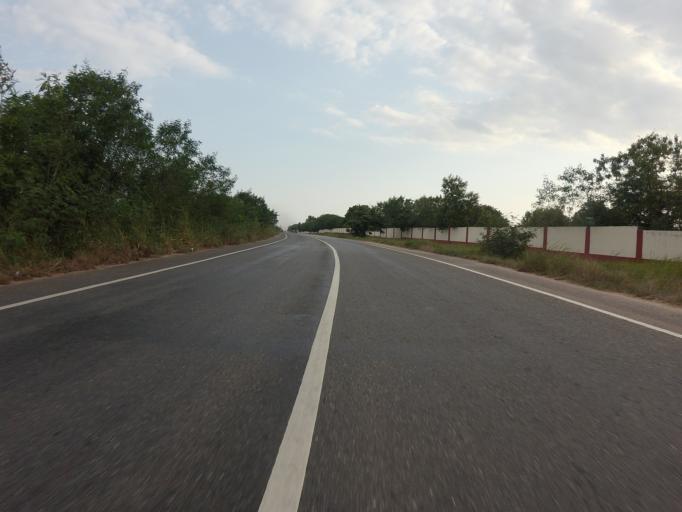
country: GH
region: Volta
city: Anloga
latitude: 6.0968
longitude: 0.5087
